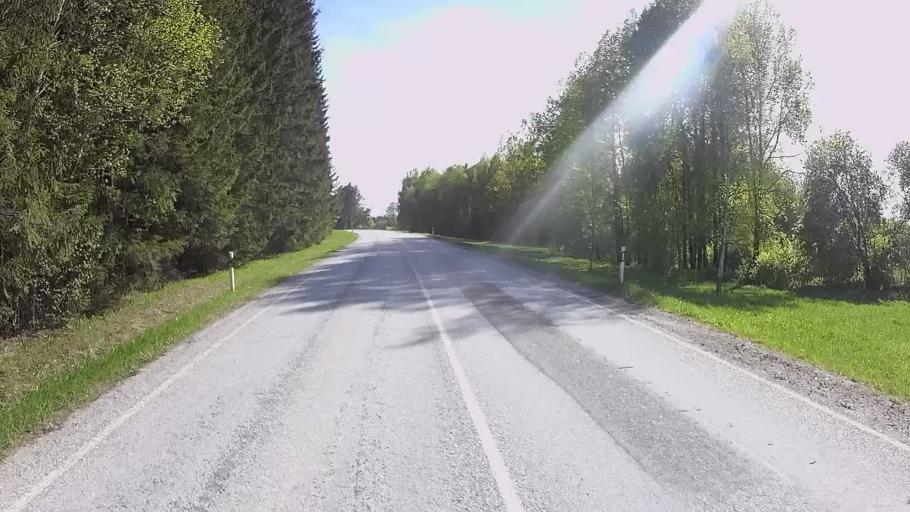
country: EE
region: Vorumaa
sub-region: Antsla vald
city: Vana-Antsla
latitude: 58.0158
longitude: 26.4989
